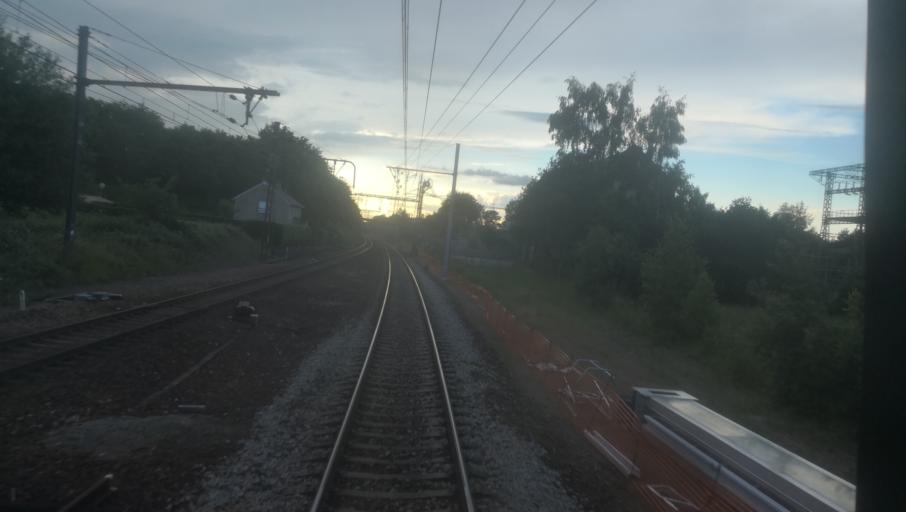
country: FR
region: Limousin
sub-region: Departement de la Creuse
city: La Souterraine
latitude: 46.2460
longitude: 1.4869
